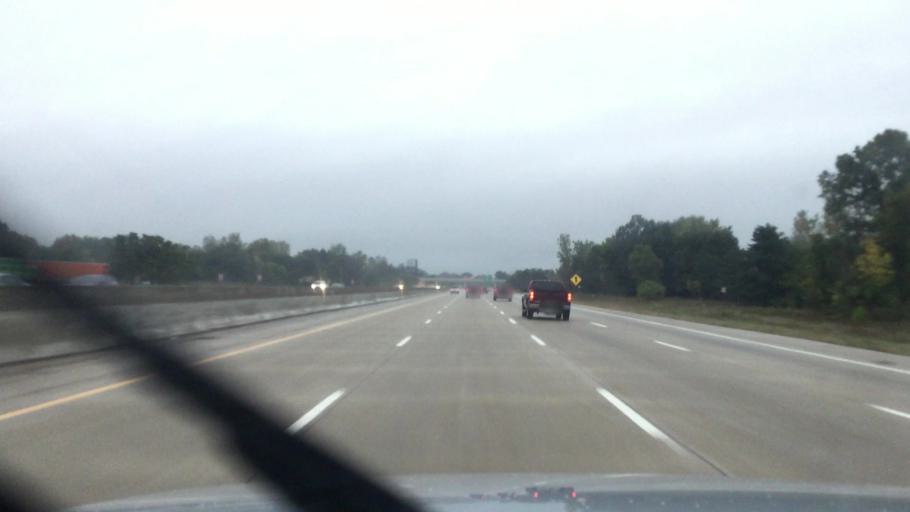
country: US
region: Michigan
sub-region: Genesee County
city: Clio
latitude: 43.1568
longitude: -83.7660
